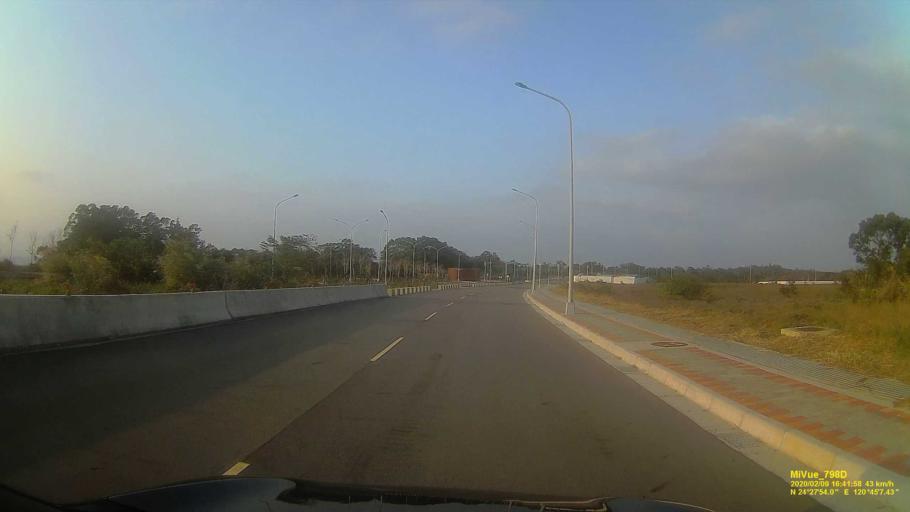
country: TW
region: Taiwan
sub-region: Miaoli
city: Miaoli
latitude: 24.4652
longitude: 120.7521
